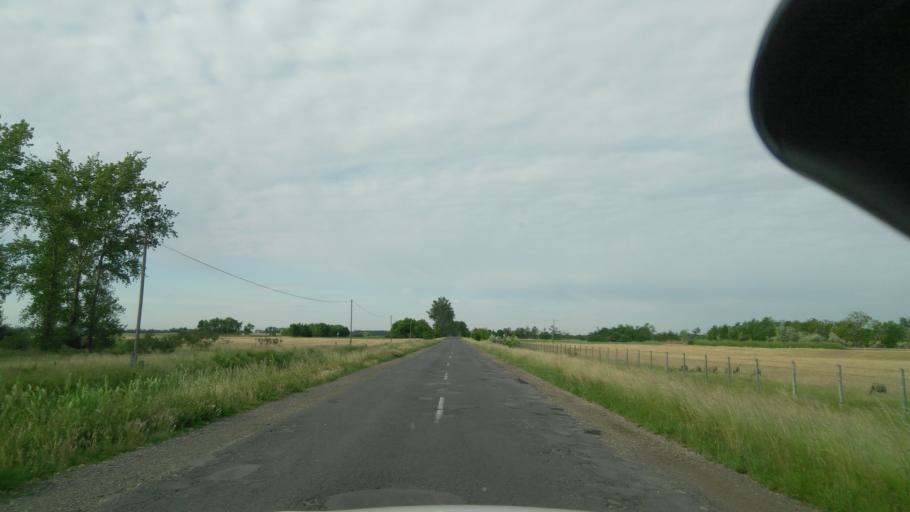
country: HU
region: Bekes
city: Gyula
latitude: 46.6089
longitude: 21.2454
